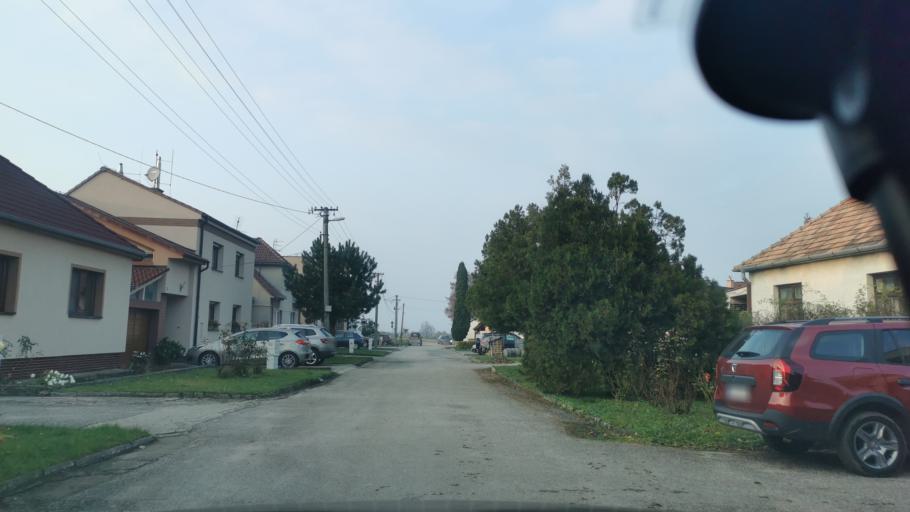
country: SK
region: Trnavsky
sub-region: Okres Skalica
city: Holic
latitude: 48.8000
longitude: 17.1869
